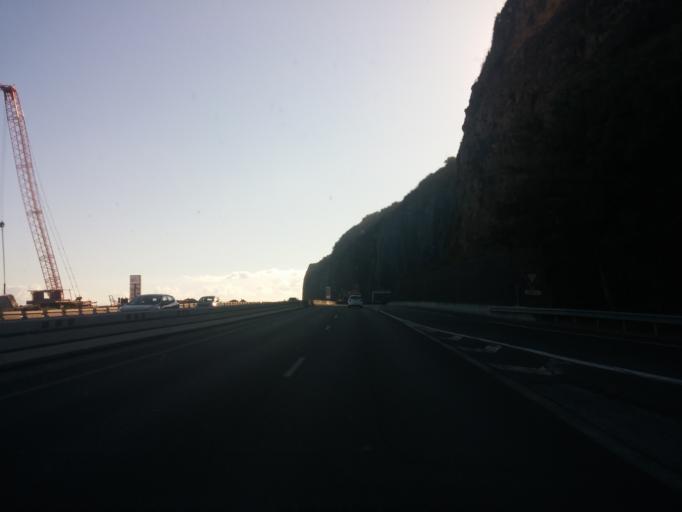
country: RE
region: Reunion
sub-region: Reunion
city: La Possession
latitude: -20.9215
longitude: 55.3458
